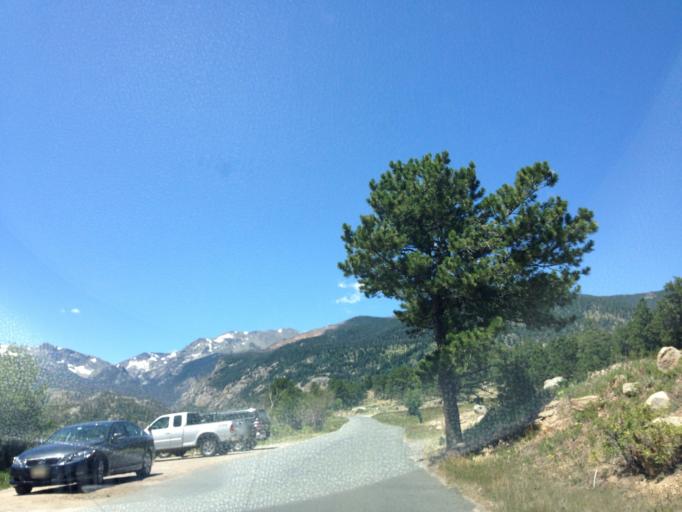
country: US
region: Colorado
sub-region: Larimer County
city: Estes Park
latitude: 40.3567
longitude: -105.5996
